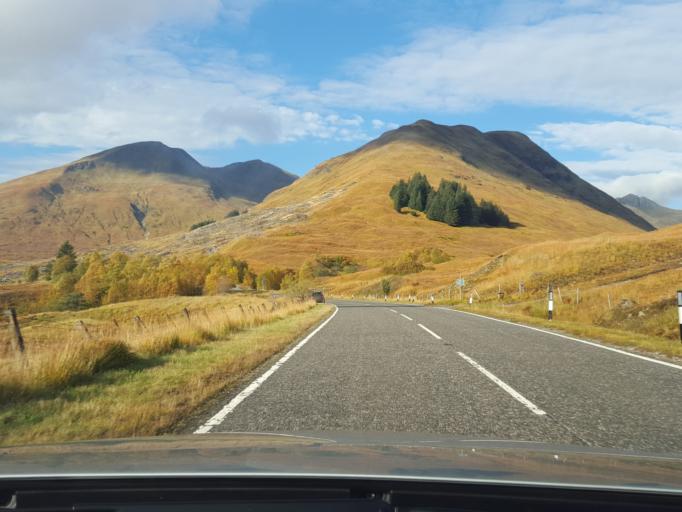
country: GB
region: Scotland
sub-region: Highland
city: Fort William
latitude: 57.1593
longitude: -5.1561
